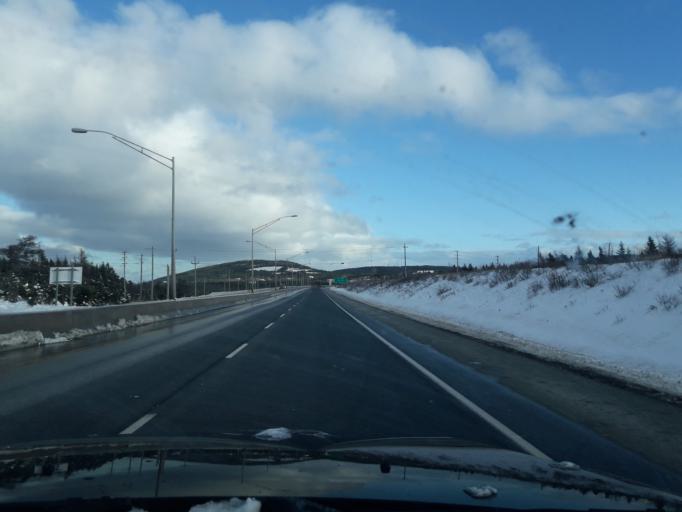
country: CA
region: Newfoundland and Labrador
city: St. John's
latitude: 47.6132
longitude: -52.7034
